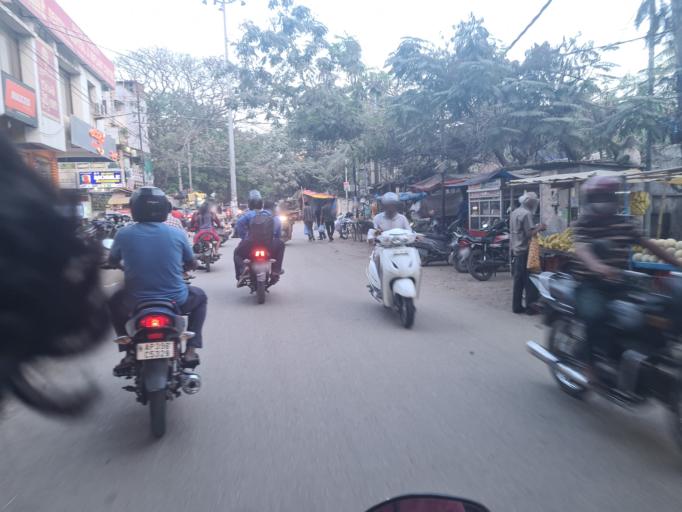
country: IN
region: Telangana
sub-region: Medak
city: Serilingampalle
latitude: 17.4941
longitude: 78.3247
